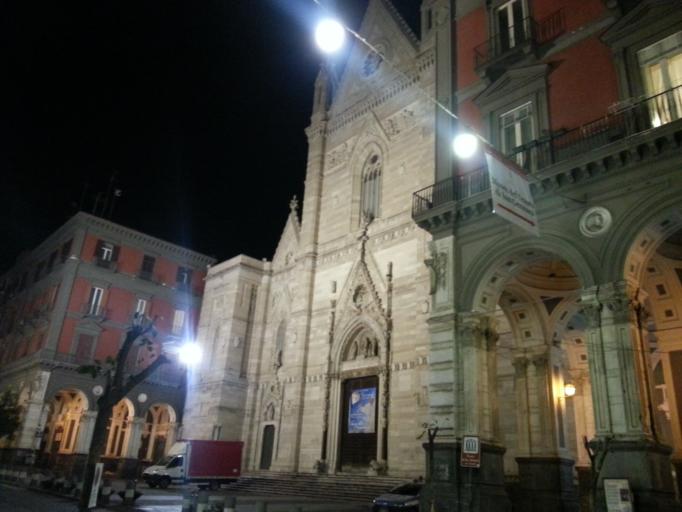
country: IT
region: Campania
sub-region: Provincia di Napoli
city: Napoli
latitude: 40.8517
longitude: 14.2591
